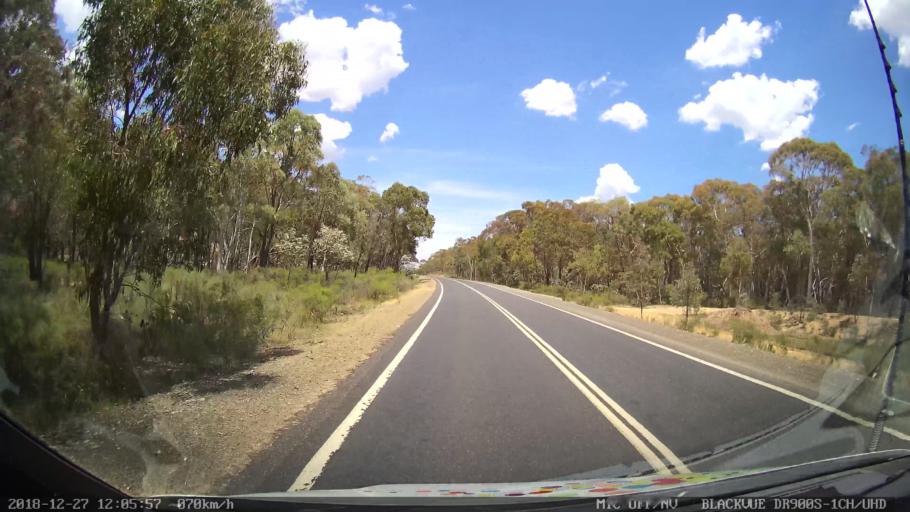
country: AU
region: New South Wales
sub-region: Blayney
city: Blayney
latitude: -33.8048
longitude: 149.3328
